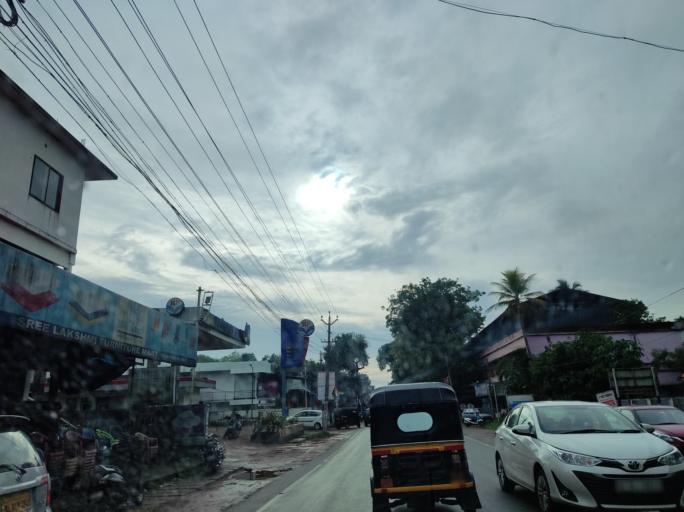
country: IN
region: Kerala
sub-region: Alappuzha
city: Kattanam
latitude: 9.1749
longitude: 76.6402
